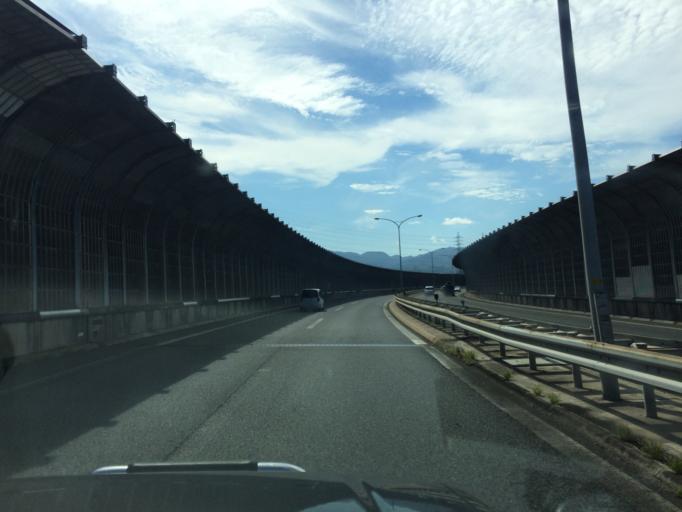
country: JP
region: Osaka
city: Izumi
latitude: 34.4703
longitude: 135.4648
